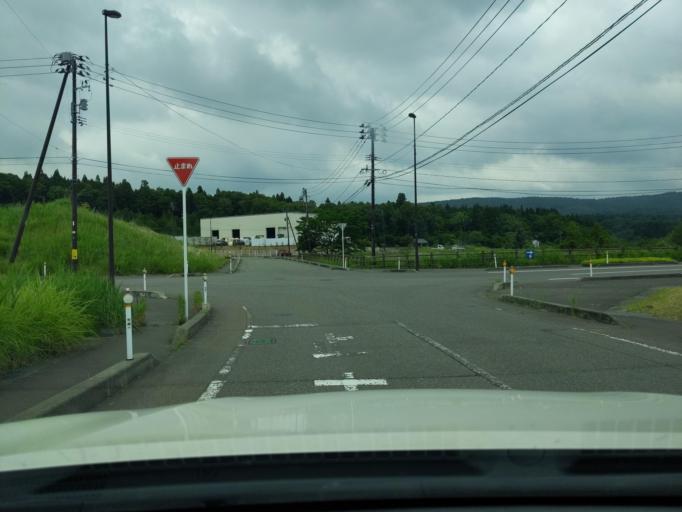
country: JP
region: Niigata
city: Kashiwazaki
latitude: 37.3387
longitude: 138.5880
